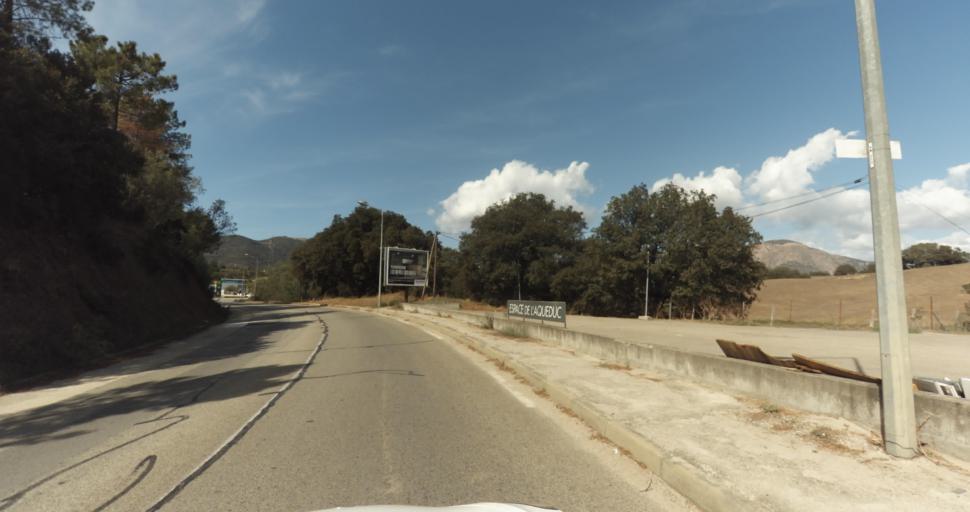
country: FR
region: Corsica
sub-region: Departement de la Corse-du-Sud
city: Afa
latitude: 41.9553
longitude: 8.7837
